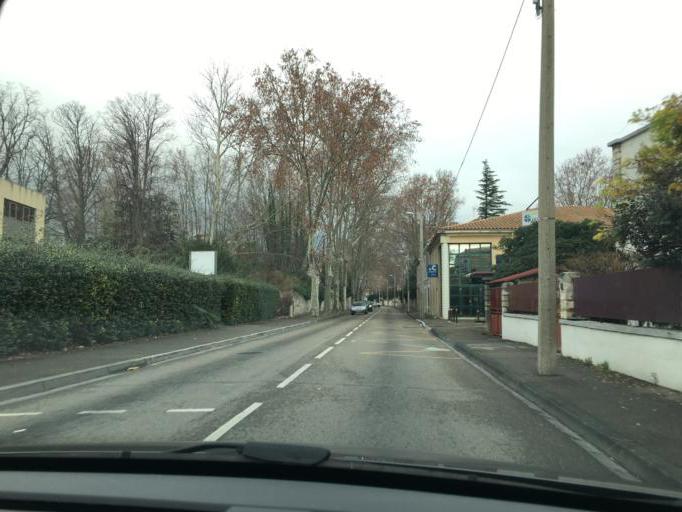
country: FR
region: Provence-Alpes-Cote d'Azur
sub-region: Departement du Vaucluse
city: Avignon
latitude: 43.9316
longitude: 4.8097
